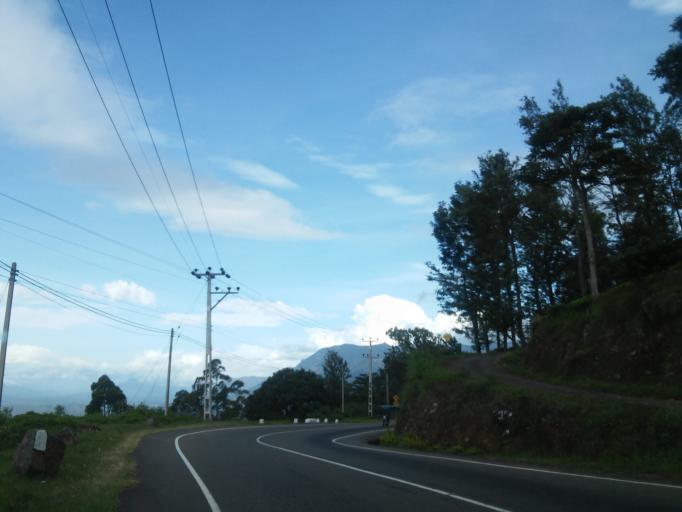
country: LK
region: Uva
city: Haputale
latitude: 6.7620
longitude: 80.9276
